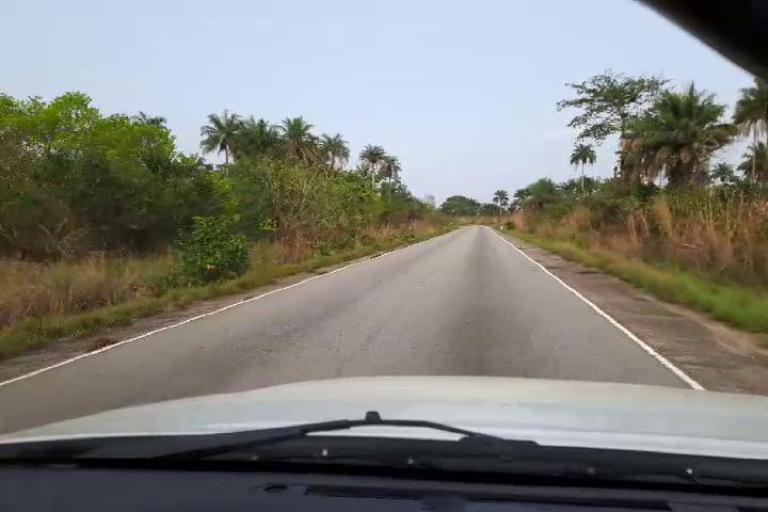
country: SL
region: Southern Province
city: Baoma
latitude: 7.9253
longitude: -11.5354
